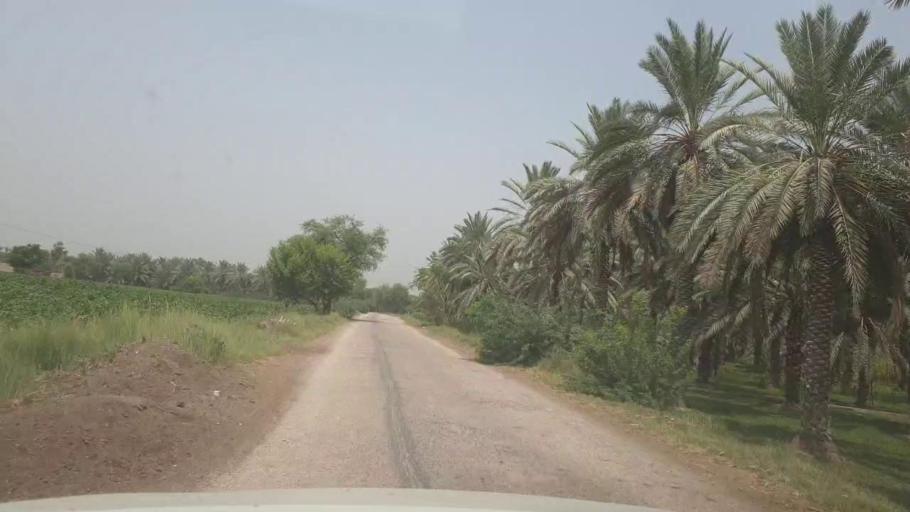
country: PK
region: Sindh
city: Kot Diji
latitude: 27.3651
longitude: 68.6532
